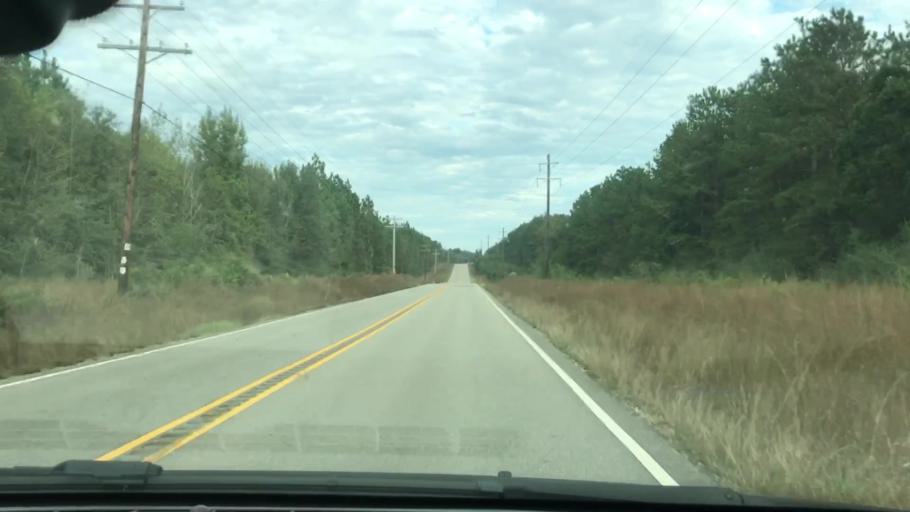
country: US
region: Louisiana
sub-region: Saint Tammany Parish
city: Abita Springs
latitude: 30.5270
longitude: -89.9194
